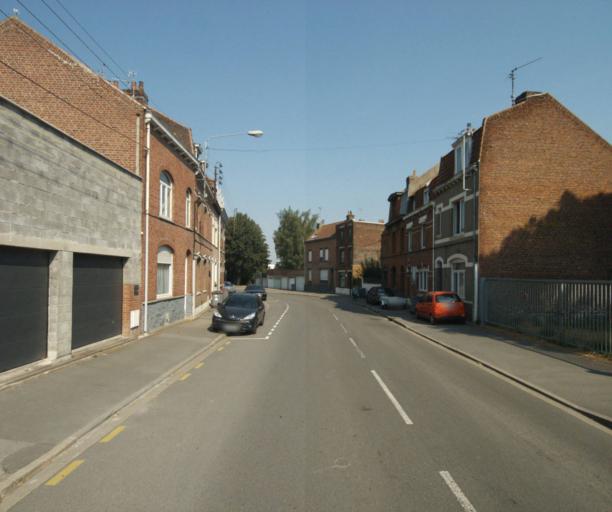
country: FR
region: Nord-Pas-de-Calais
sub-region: Departement du Nord
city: Quesnoy-sur-Deule
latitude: 50.7095
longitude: 3.0001
